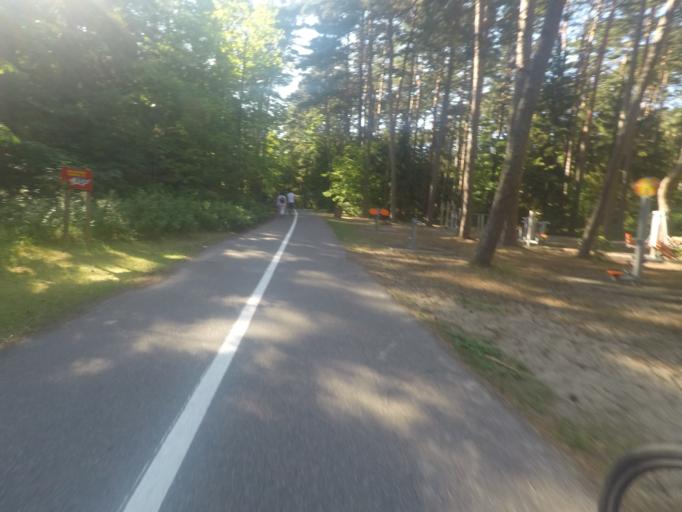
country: LT
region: Klaipedos apskritis
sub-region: Klaipeda
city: Klaipeda
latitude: 55.5451
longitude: 21.1175
